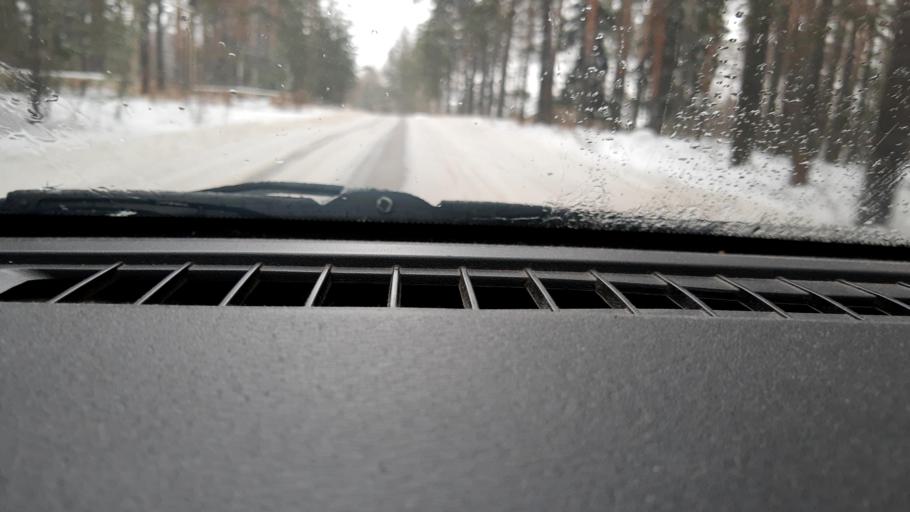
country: RU
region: Nizjnij Novgorod
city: Afonino
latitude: 56.1847
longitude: 44.0797
